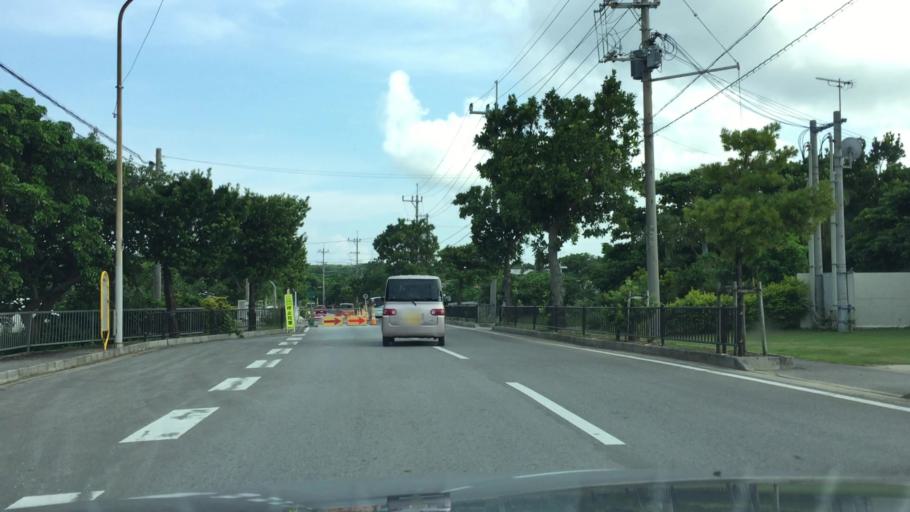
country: JP
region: Okinawa
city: Ishigaki
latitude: 24.4555
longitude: 124.2484
